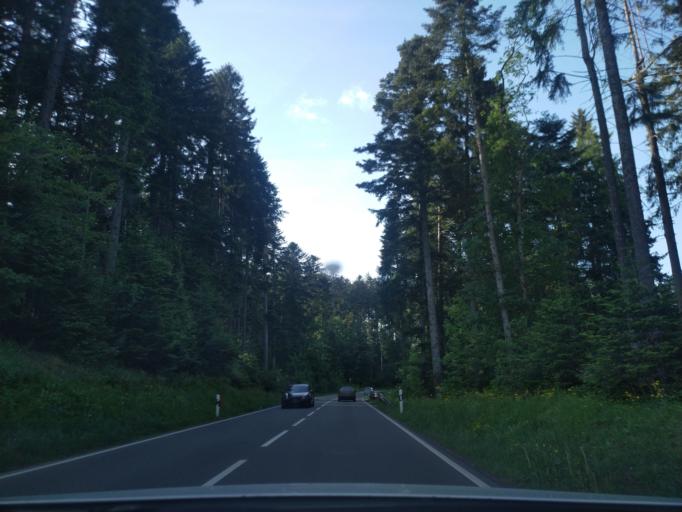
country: DE
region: Baden-Wuerttemberg
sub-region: Karlsruhe Region
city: Lossburg
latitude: 48.4257
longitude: 8.4438
